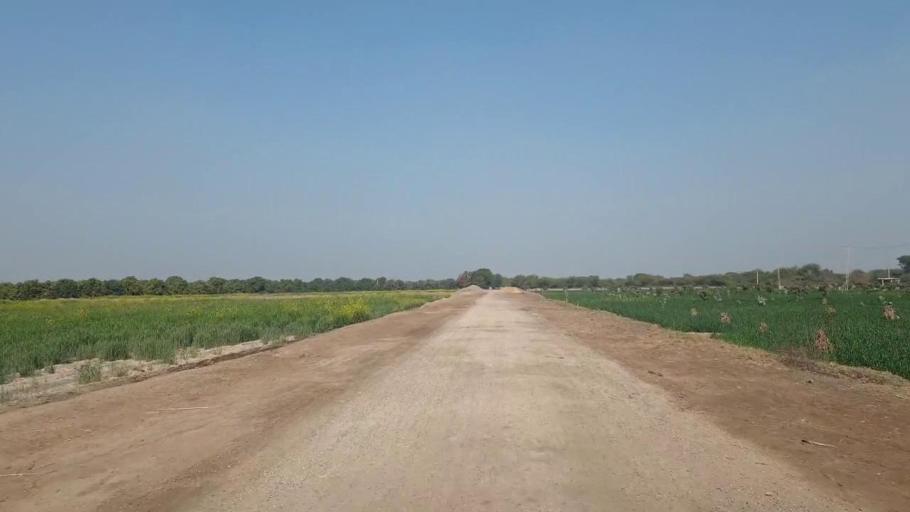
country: PK
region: Sindh
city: Mirwah Gorchani
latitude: 25.3809
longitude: 68.9318
